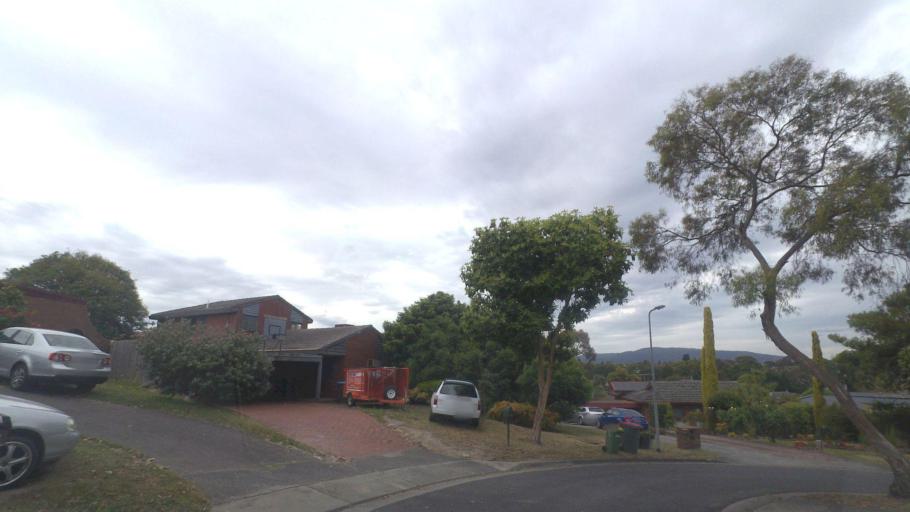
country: AU
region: Victoria
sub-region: Knox
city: Wantirna
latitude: -37.8580
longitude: 145.2374
